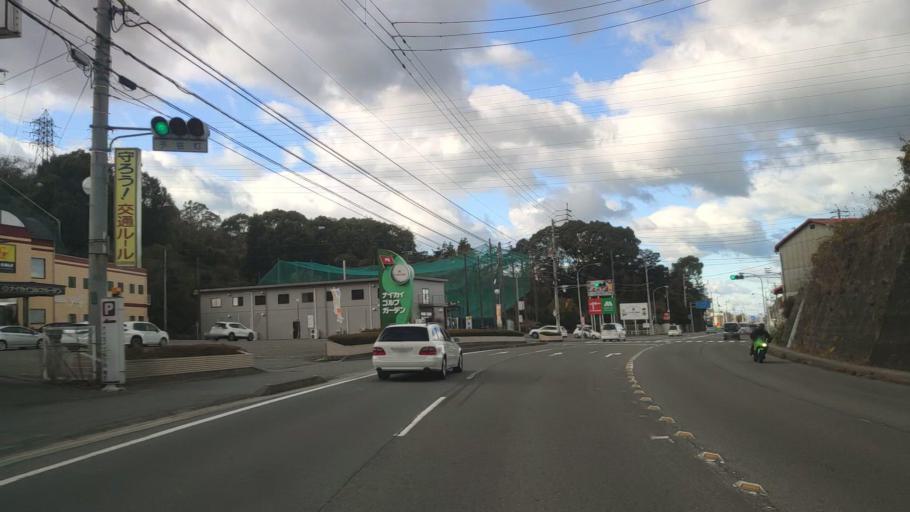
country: JP
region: Ehime
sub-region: Shikoku-chuo Shi
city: Matsuyama
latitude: 33.8561
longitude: 132.7355
